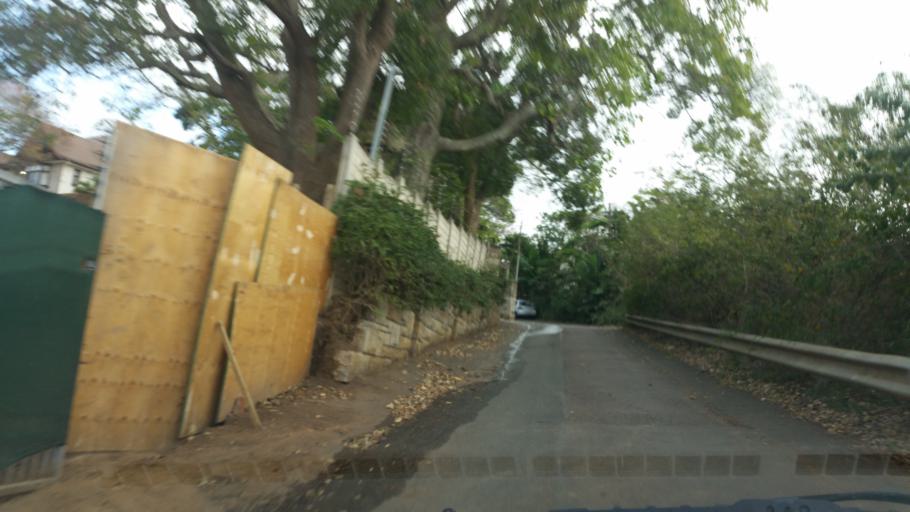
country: ZA
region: KwaZulu-Natal
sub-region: eThekwini Metropolitan Municipality
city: Berea
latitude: -29.8304
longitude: 30.9215
